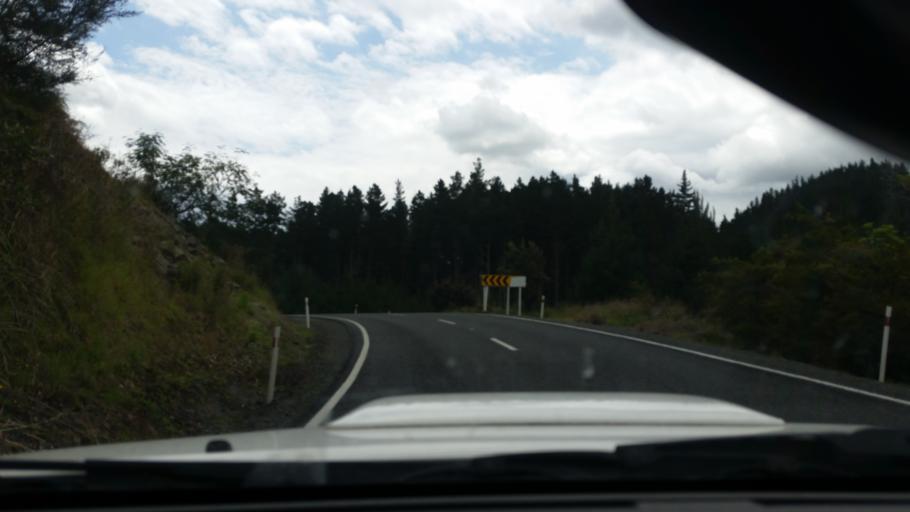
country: NZ
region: Northland
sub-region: Kaipara District
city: Dargaville
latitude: -35.7372
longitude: 173.8673
